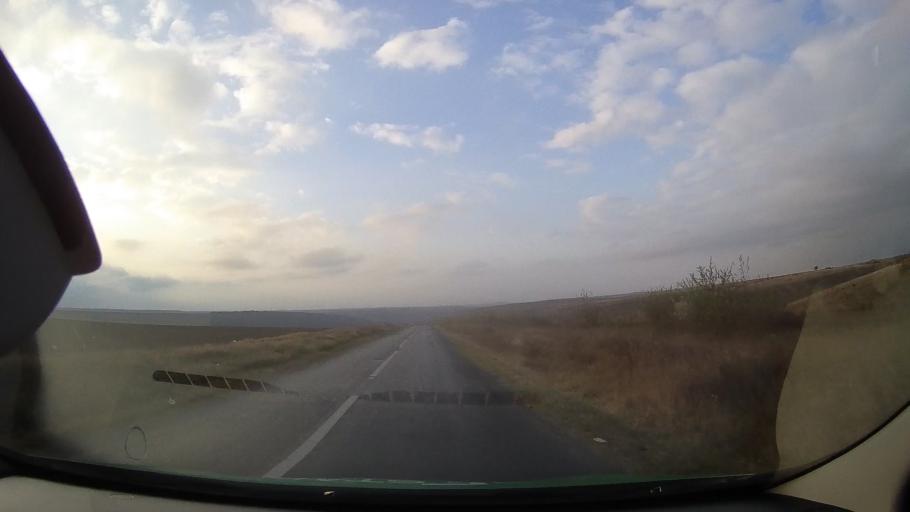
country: RO
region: Constanta
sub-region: Comuna Adamclisi
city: Adamclisi
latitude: 44.0191
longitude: 27.8879
